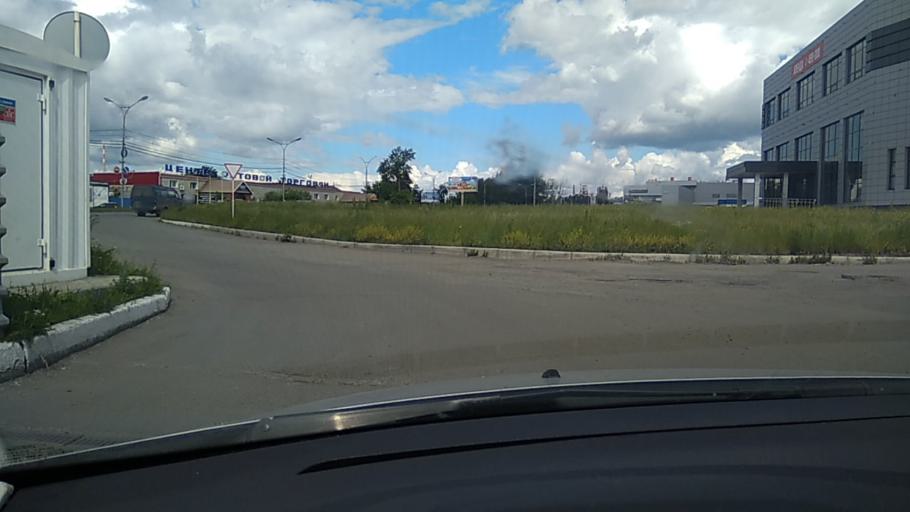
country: RU
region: Sverdlovsk
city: Nizhniy Tagil
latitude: 57.9057
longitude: 60.0104
